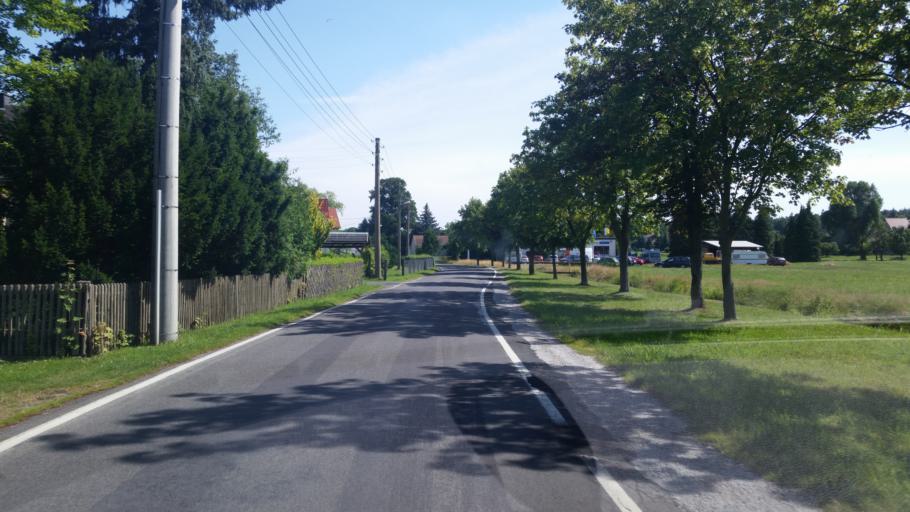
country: DE
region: Saxony
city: Schwepnitz
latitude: 51.3301
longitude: 14.0111
